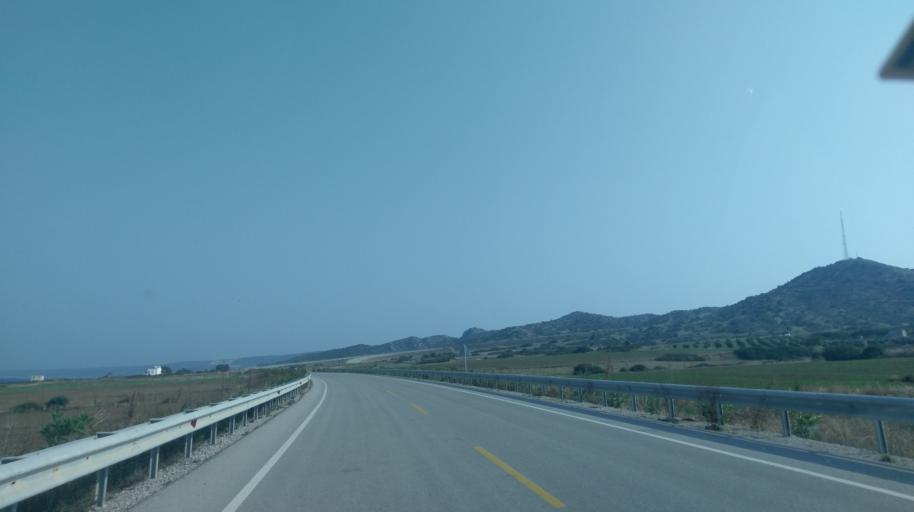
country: CY
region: Ammochostos
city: Leonarisso
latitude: 35.4919
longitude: 34.0879
